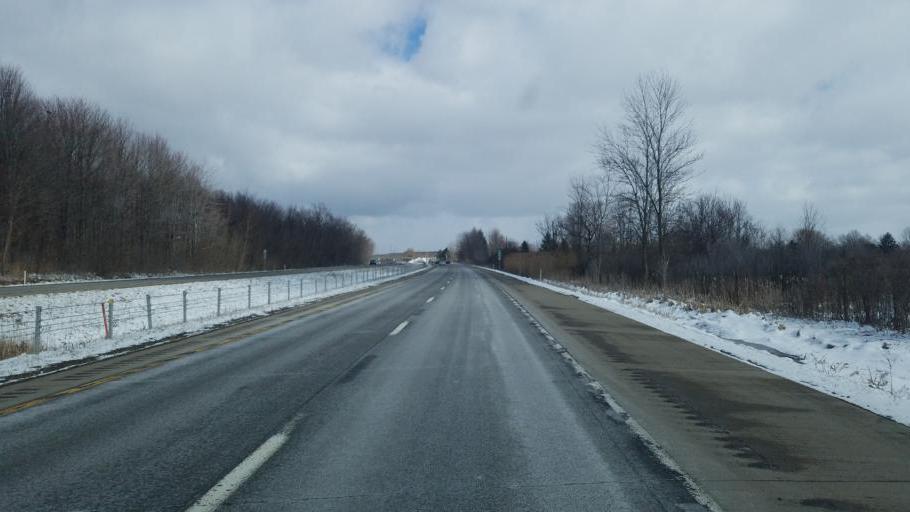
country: US
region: Pennsylvania
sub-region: Erie County
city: Fairview
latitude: 42.0244
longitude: -80.1399
